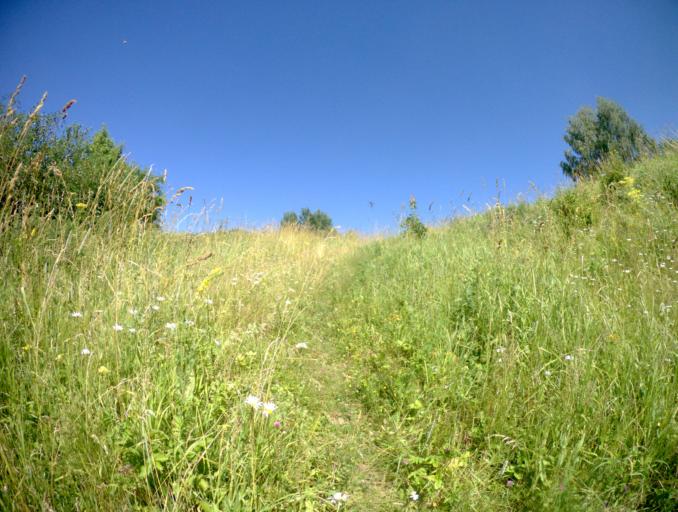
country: RU
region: Nizjnij Novgorod
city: Gorbatov
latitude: 56.0833
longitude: 43.0816
